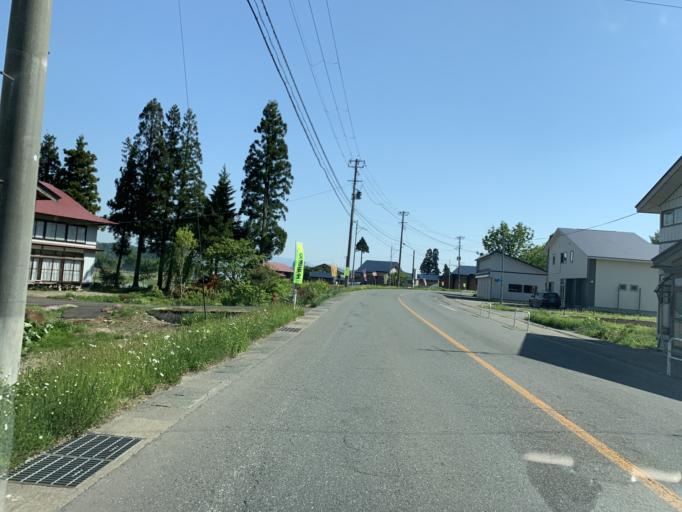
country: JP
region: Akita
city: Yokotemachi
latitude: 39.4291
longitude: 140.7505
